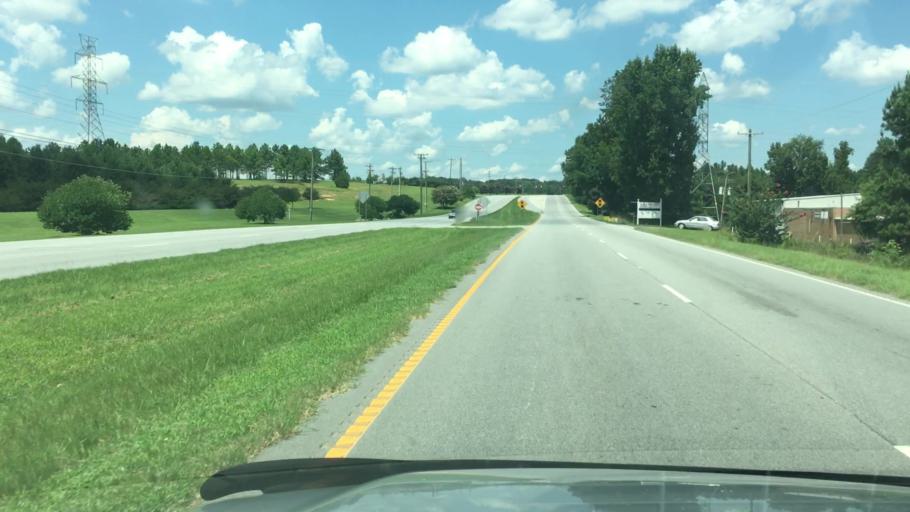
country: US
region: South Carolina
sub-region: Spartanburg County
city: Roebuck
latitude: 34.8488
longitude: -81.9673
